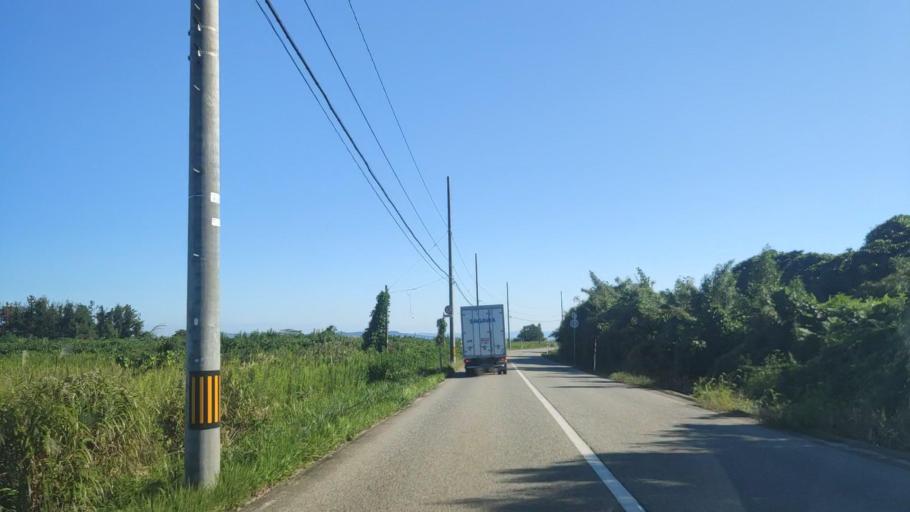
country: JP
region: Ishikawa
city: Nanao
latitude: 37.1959
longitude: 136.9106
